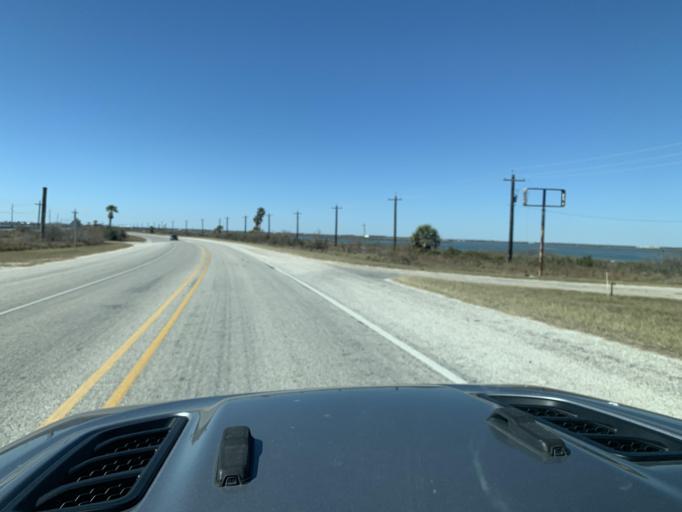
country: US
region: Texas
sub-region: San Patricio County
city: Aransas Pass
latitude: 27.8902
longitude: -97.1119
